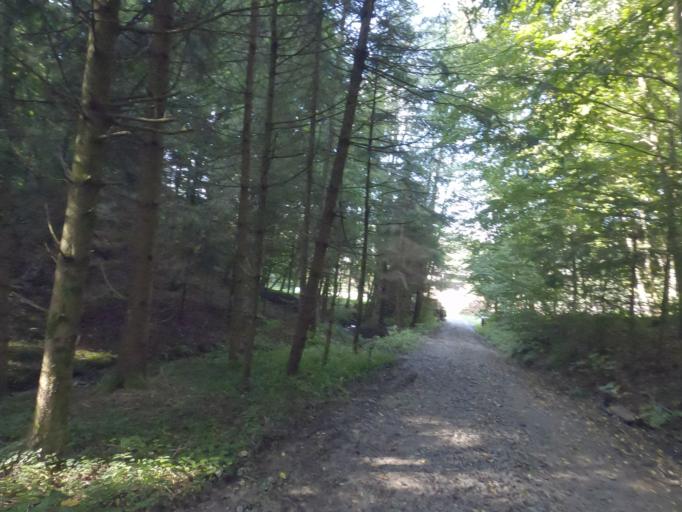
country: DE
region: Bavaria
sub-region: Lower Bavaria
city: Niederalteich
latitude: 48.8136
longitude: 13.0112
